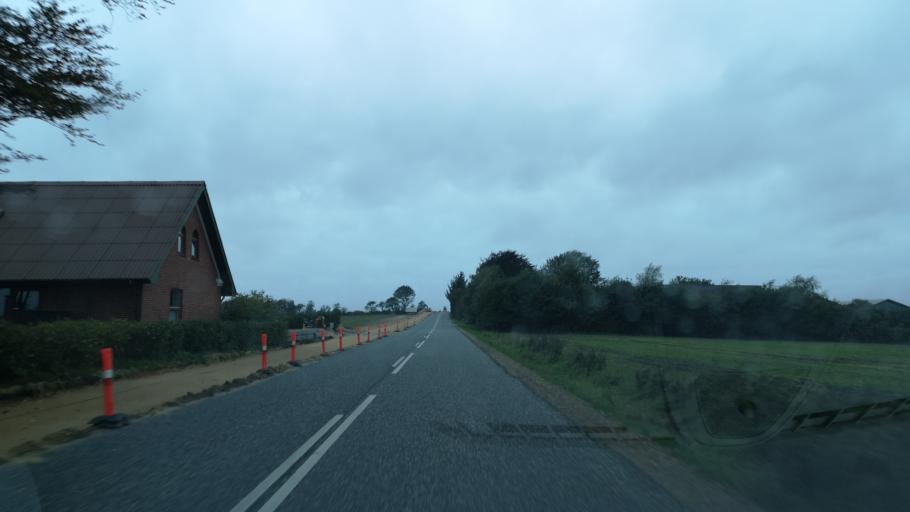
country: DK
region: Central Jutland
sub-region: Ringkobing-Skjern Kommune
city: Videbaek
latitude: 56.0534
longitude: 8.6448
